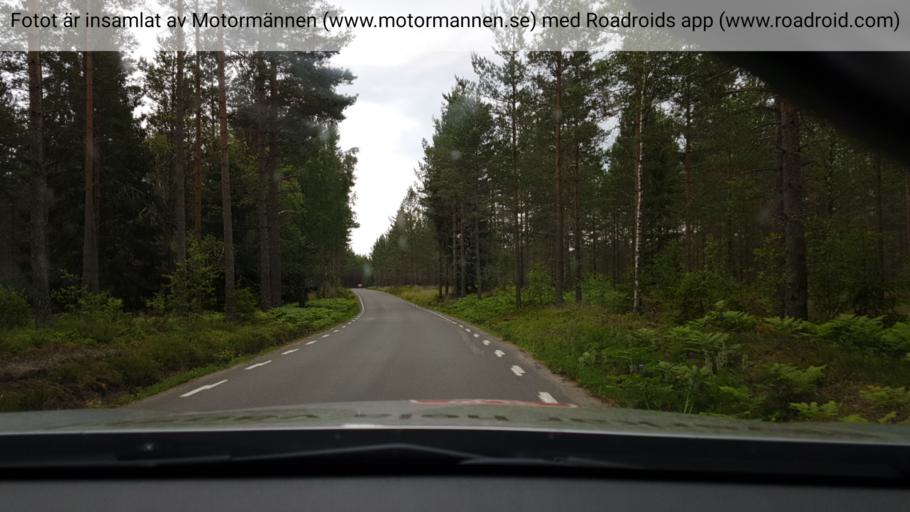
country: SE
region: Vaestra Goetaland
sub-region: Tidaholms Kommun
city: Tidaholm
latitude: 58.0866
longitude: 14.0717
